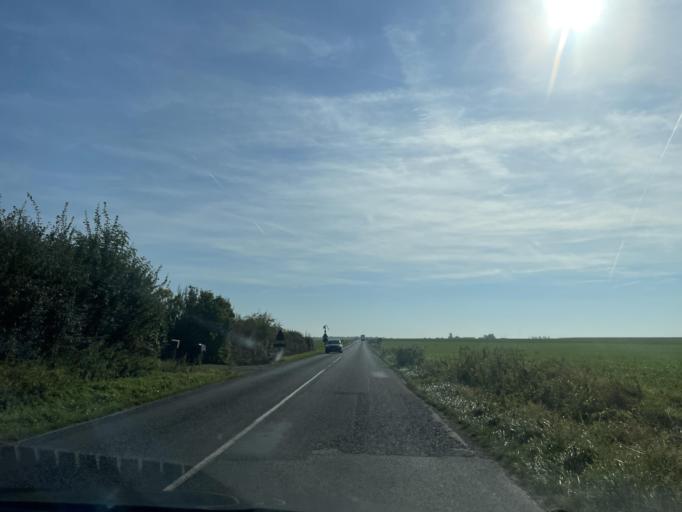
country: FR
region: Ile-de-France
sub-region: Departement de Seine-et-Marne
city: Coulommiers
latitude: 48.8765
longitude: 3.0799
